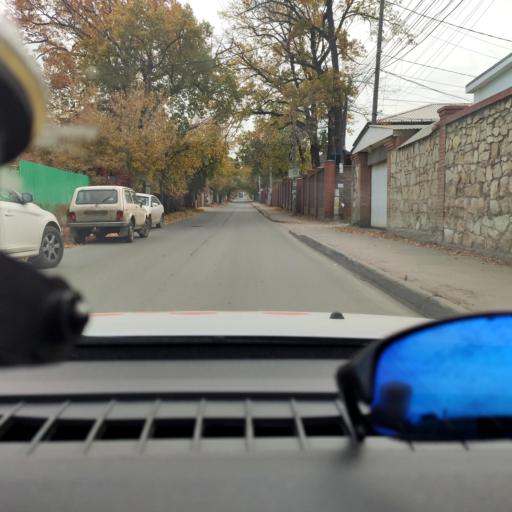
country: RU
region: Samara
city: Samara
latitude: 53.2559
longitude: 50.1889
